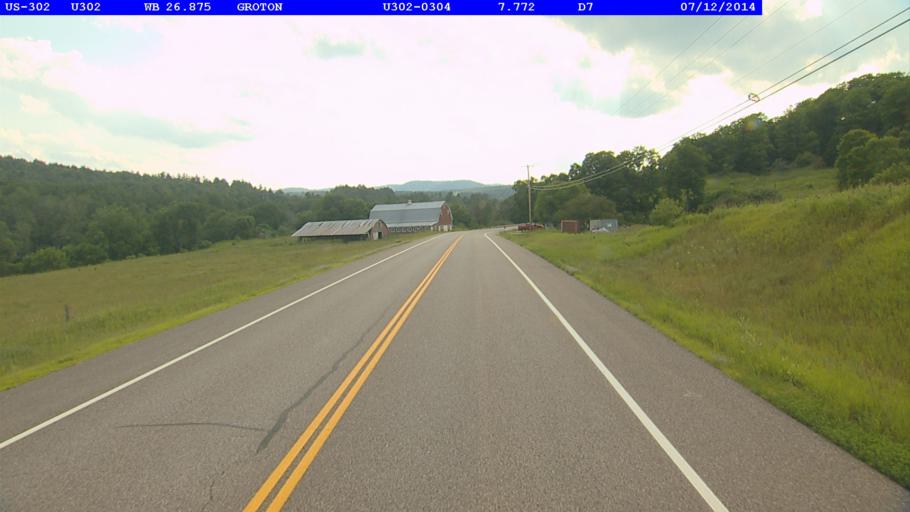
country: US
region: New Hampshire
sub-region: Grafton County
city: Woodsville
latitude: 44.2053
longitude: -72.1725
